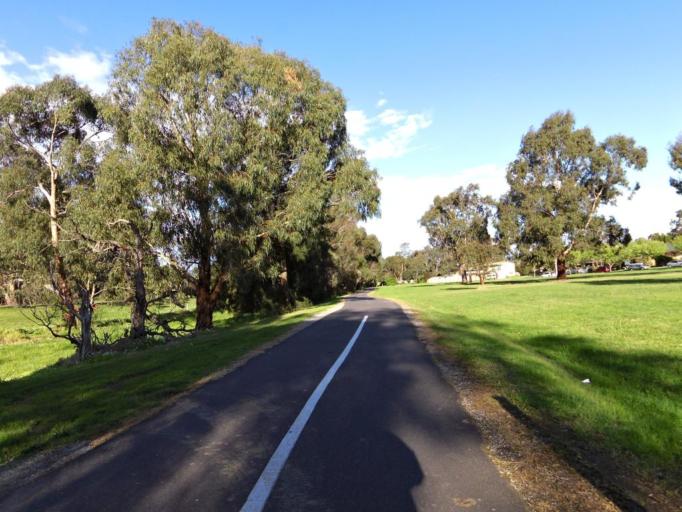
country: AU
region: Victoria
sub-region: Knox
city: Wantirna
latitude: -37.8381
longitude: 145.2230
